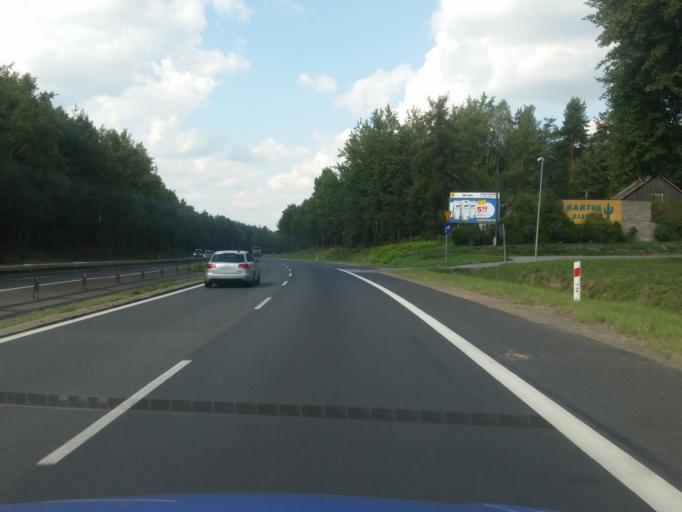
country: PL
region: Silesian Voivodeship
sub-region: Powiat czestochowski
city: Kamienica Polska
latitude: 50.6617
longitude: 19.1288
